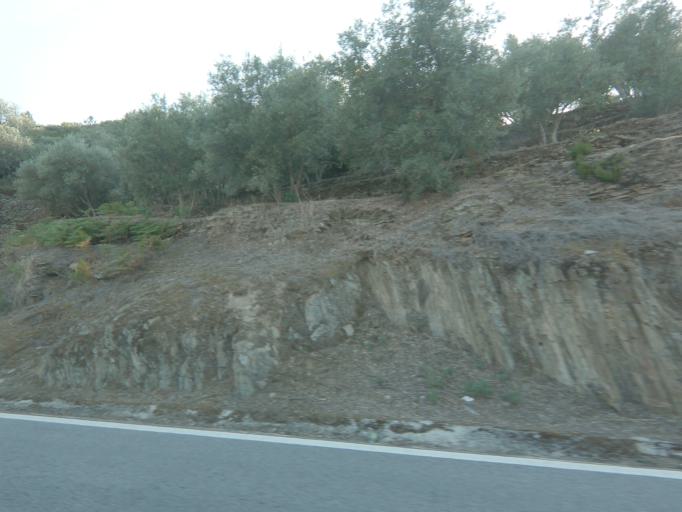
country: PT
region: Viseu
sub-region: Tabuaco
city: Tabuaco
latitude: 41.1292
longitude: -7.5676
